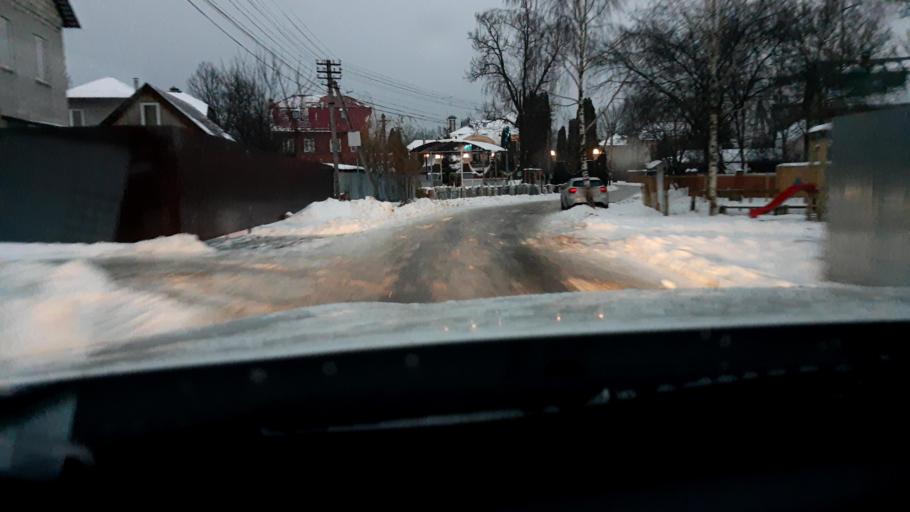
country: RU
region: Moskovskaya
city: Kommunarka
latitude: 55.5941
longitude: 37.4858
